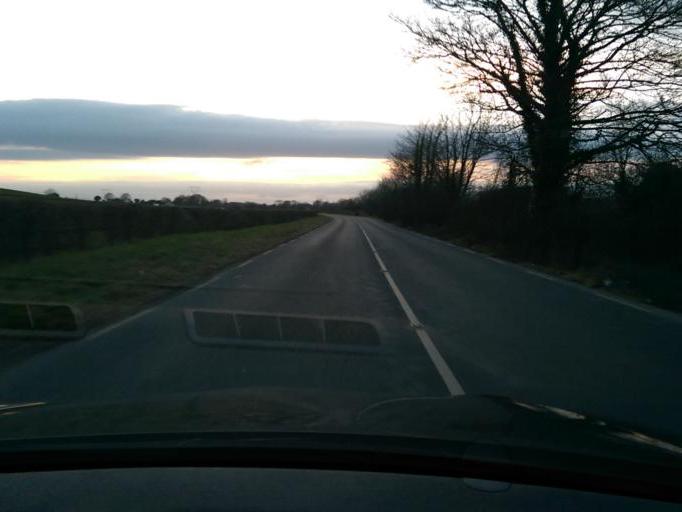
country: IE
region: Leinster
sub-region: Uibh Fhaili
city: Banagher
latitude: 53.1065
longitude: -8.0353
